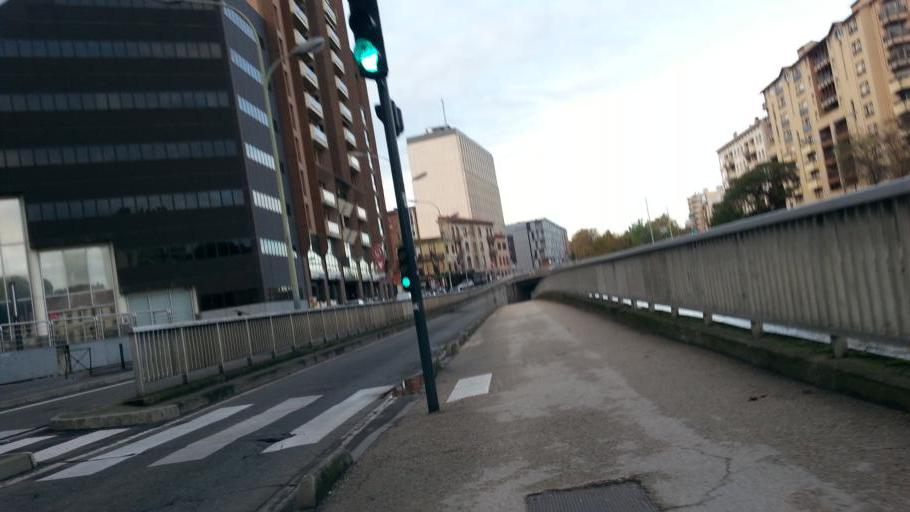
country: FR
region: Midi-Pyrenees
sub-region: Departement de la Haute-Garonne
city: Toulouse
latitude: 43.5992
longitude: 1.4564
